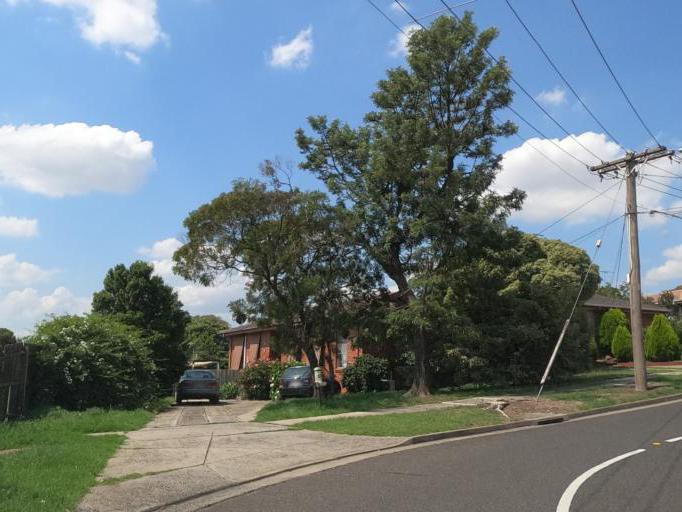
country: AU
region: Victoria
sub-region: Hume
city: Broadmeadows
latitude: -37.6718
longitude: 144.9190
